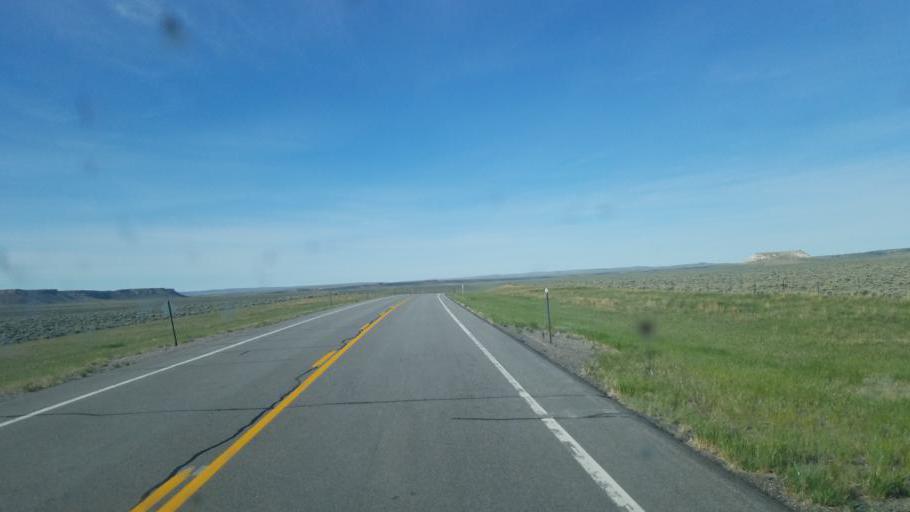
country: US
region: Wyoming
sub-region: Fremont County
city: Riverton
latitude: 42.6628
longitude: -108.1844
